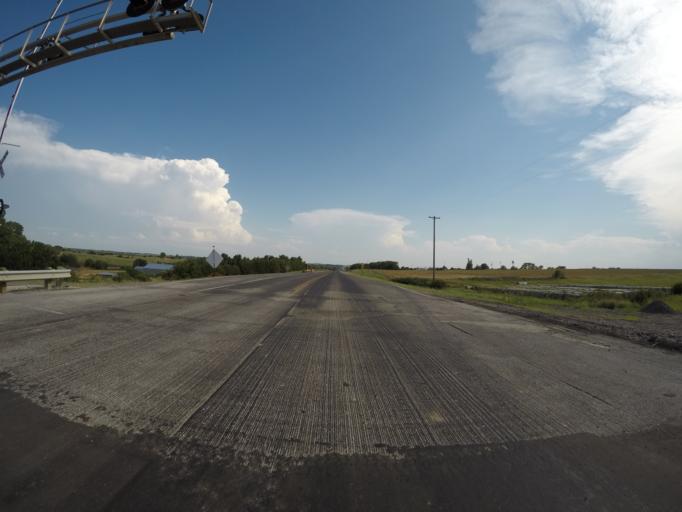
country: US
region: Kansas
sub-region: Washington County
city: Washington
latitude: 39.9035
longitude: -96.8624
